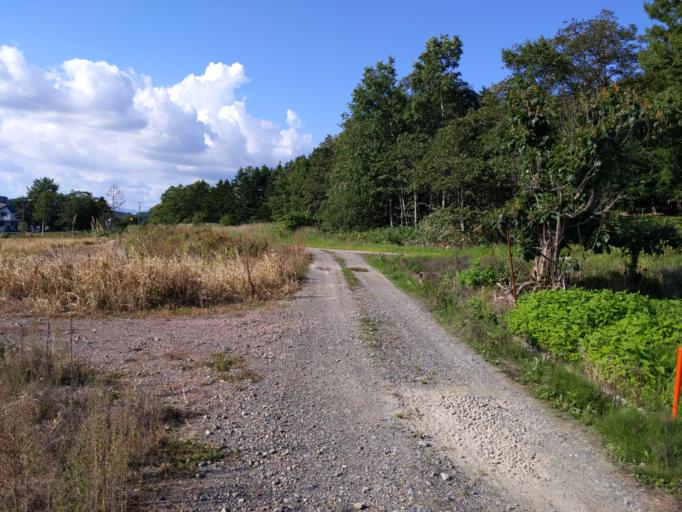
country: JP
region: Hokkaido
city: Iwamizawa
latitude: 43.1939
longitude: 141.8300
